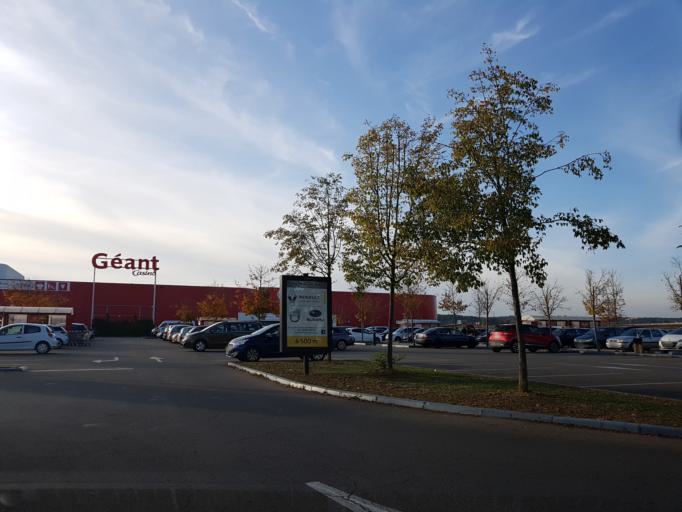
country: FR
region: Bourgogne
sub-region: Departement de la Cote-d'Or
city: Ahuy
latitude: 47.3563
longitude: 5.0329
